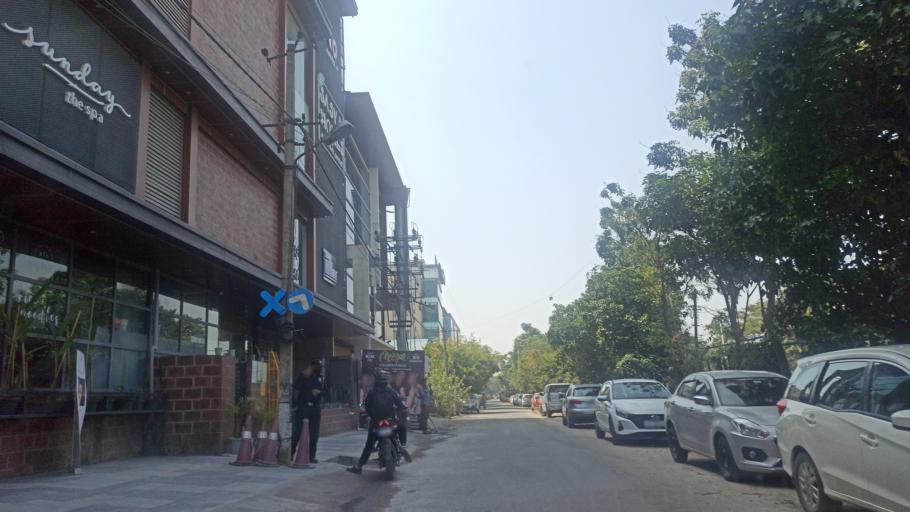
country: IN
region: Karnataka
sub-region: Bangalore Urban
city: Bangalore
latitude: 12.9158
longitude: 77.6347
